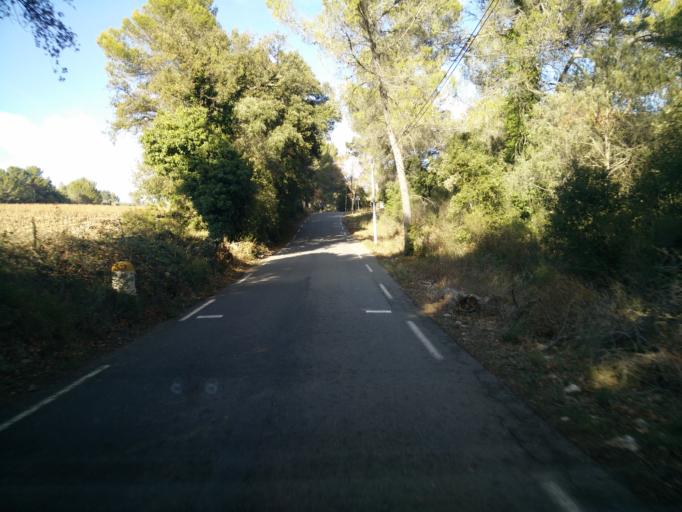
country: FR
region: Provence-Alpes-Cote d'Azur
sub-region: Departement du Var
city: Taradeau
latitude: 43.4673
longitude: 6.4319
